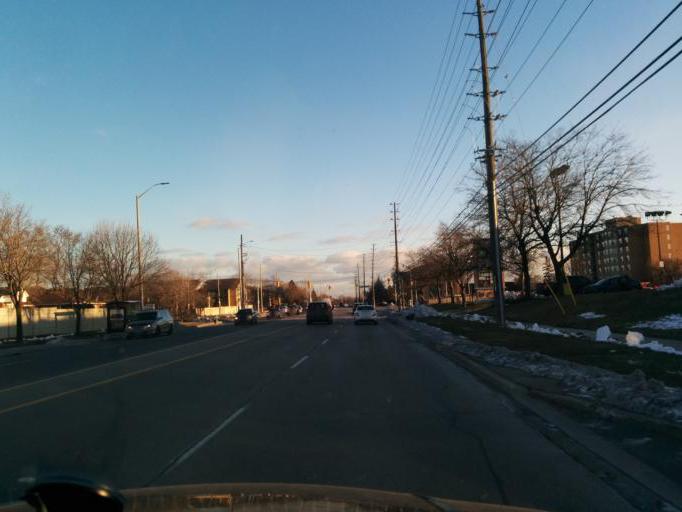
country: CA
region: Ontario
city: Mississauga
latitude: 43.6175
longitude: -79.6172
